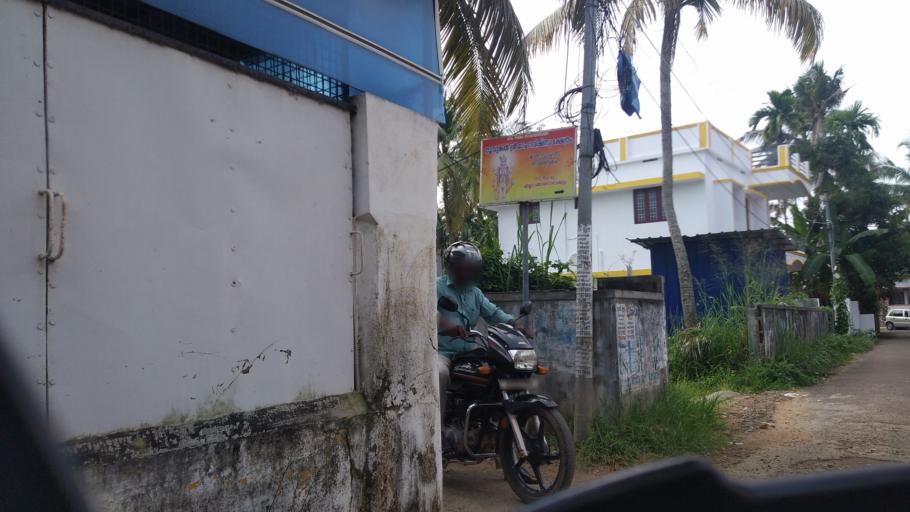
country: IN
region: Kerala
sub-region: Ernakulam
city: Elur
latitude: 10.0525
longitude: 76.2184
